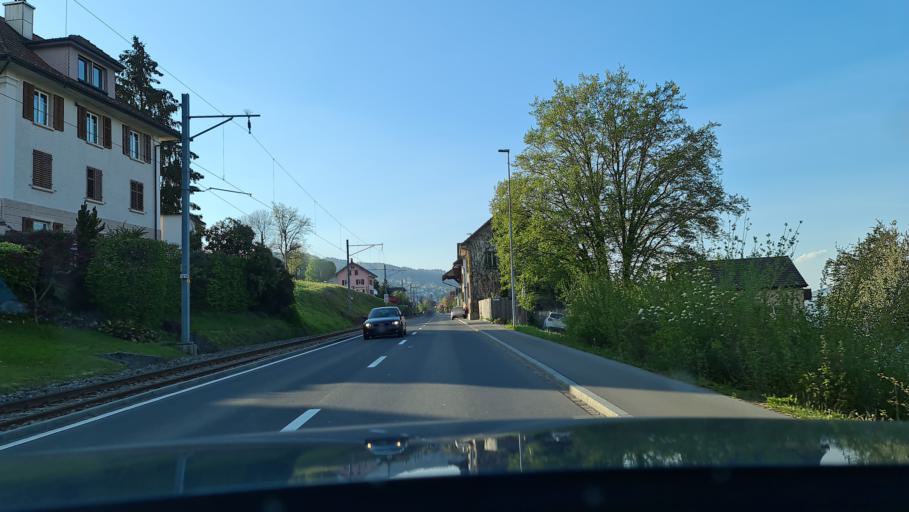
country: CH
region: Aargau
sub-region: Bezirk Kulm
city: Reinach
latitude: 47.2606
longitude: 8.2103
